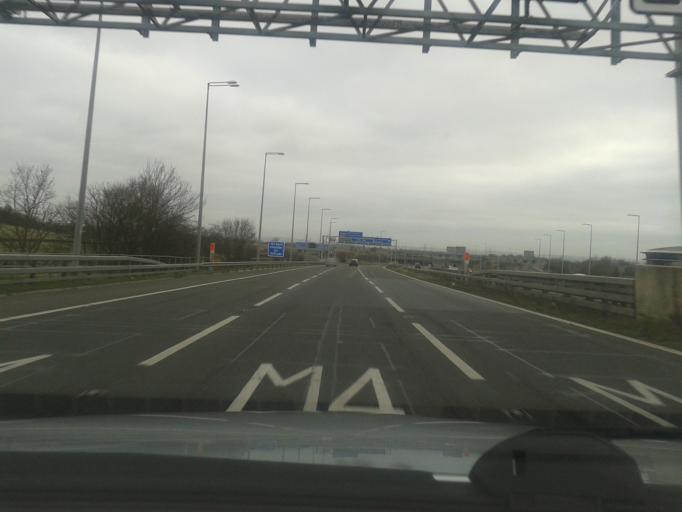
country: GB
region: England
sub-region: South Gloucestershire
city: Almondsbury
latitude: 51.5497
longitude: -2.5615
